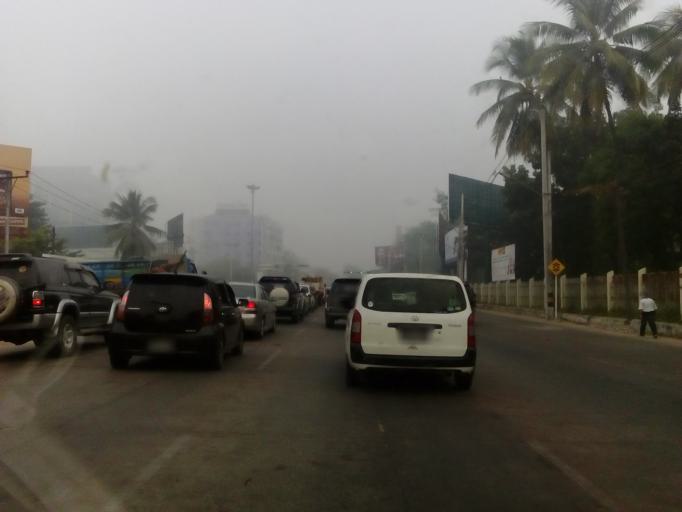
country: MM
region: Yangon
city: Yangon
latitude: 16.8212
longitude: 96.1834
